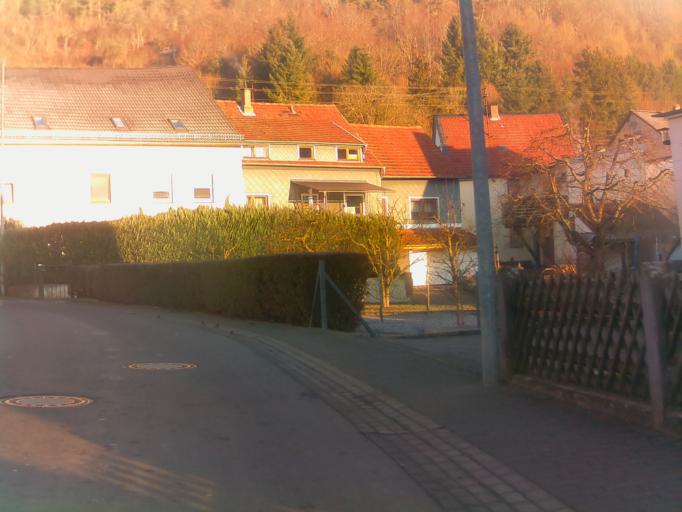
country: DE
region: Rheinland-Pfalz
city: Barenbach
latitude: 49.7634
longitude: 7.4343
